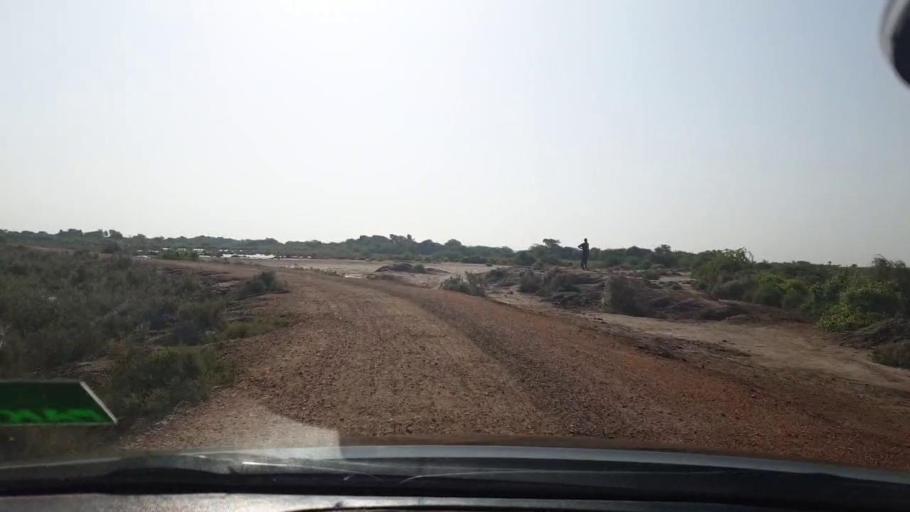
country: PK
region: Sindh
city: Tando Bago
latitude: 24.7142
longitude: 68.9716
